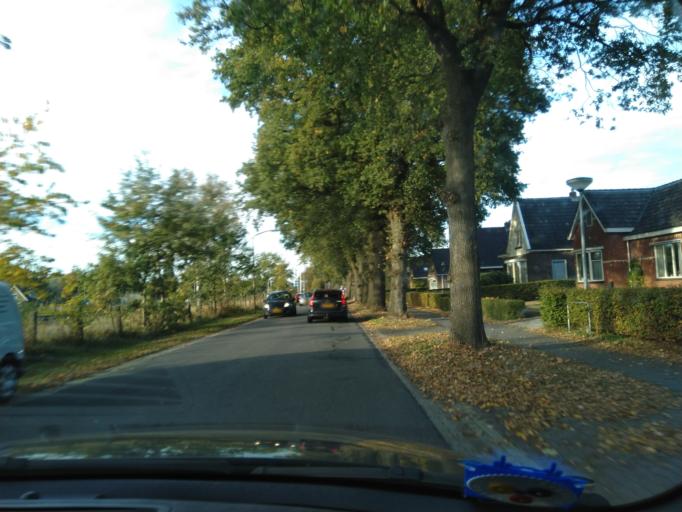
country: NL
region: Drenthe
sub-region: Gemeente Tynaarlo
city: Tynaarlo
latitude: 53.0783
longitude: 6.6283
